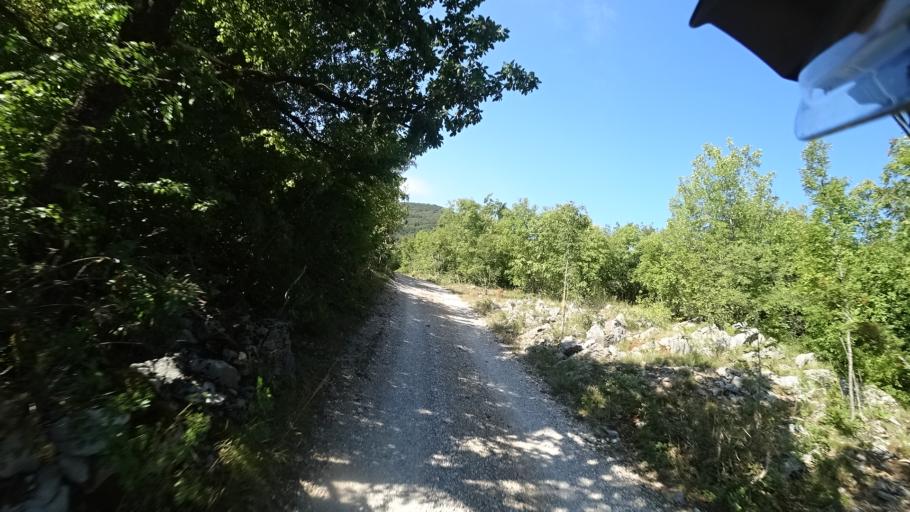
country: HR
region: Zadarska
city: Gracac
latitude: 44.2997
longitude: 16.0273
